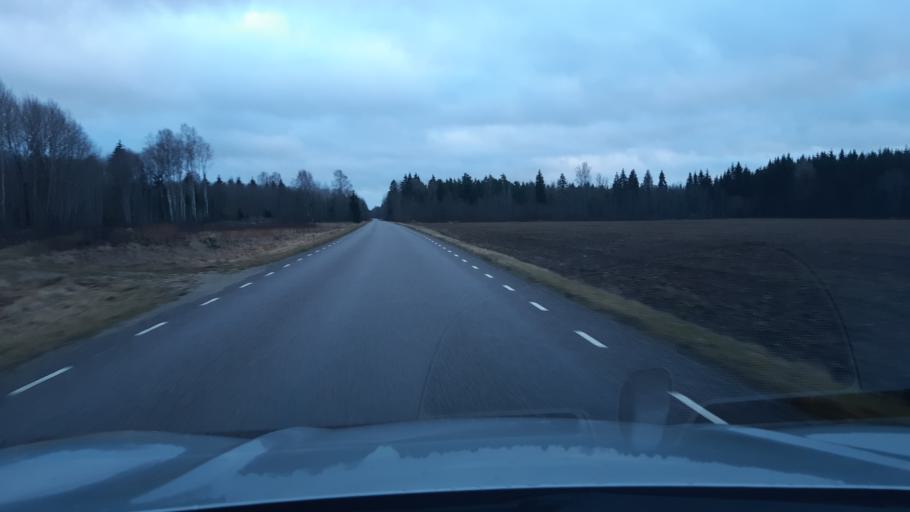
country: EE
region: Raplamaa
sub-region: Kohila vald
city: Kohila
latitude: 59.1407
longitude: 24.6551
